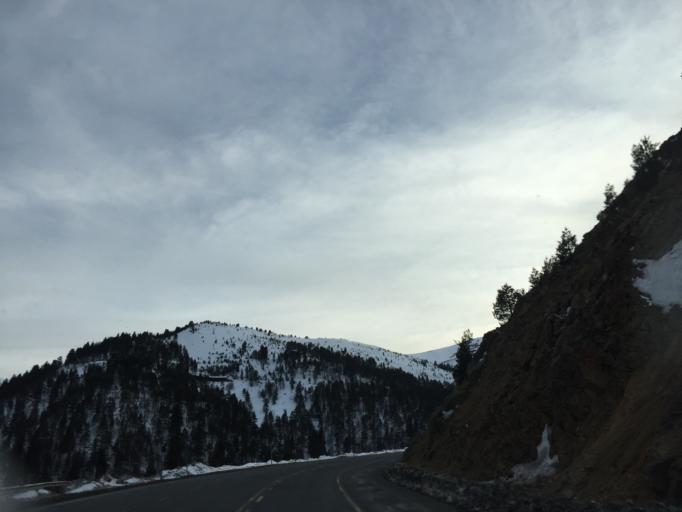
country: TR
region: Gumushane
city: Yaglidere
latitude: 40.6598
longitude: 39.4137
